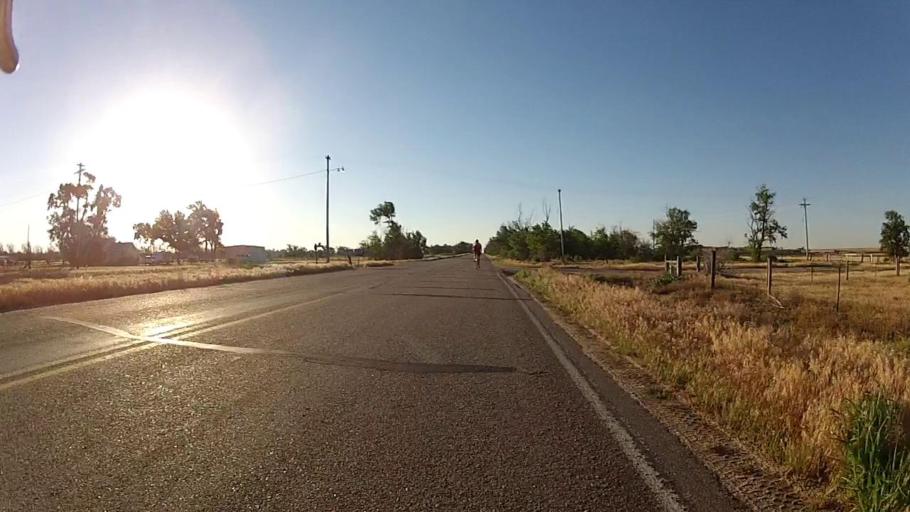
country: US
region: Kansas
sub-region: Ford County
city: Dodge City
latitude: 37.7151
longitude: -99.9328
